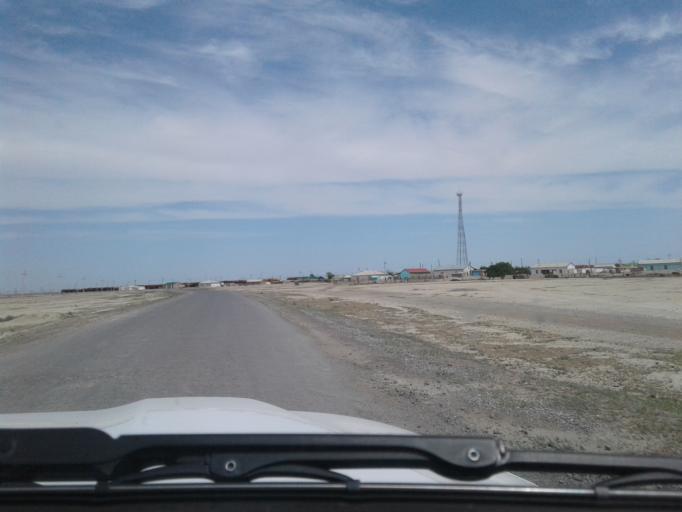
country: TM
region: Balkan
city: Gazanjyk
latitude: 39.2071
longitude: 55.7099
